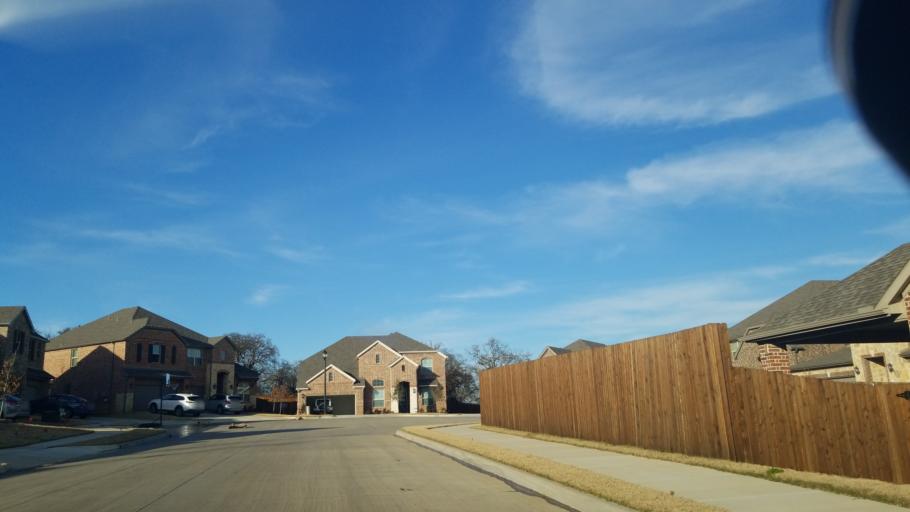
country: US
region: Texas
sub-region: Denton County
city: Corinth
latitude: 33.1464
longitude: -97.0750
